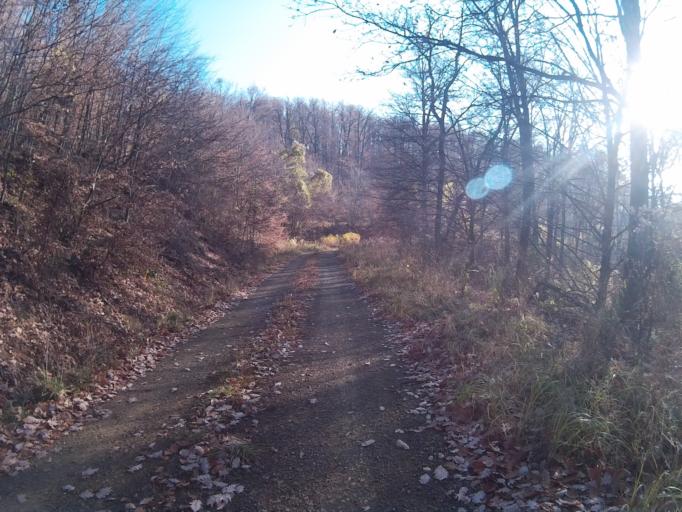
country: HU
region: Heves
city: Belapatfalva
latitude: 48.0263
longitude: 20.3763
